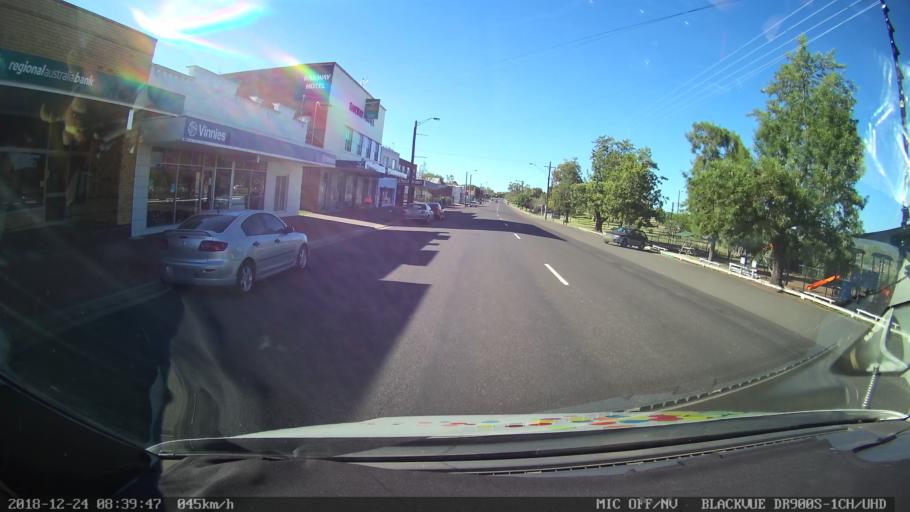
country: AU
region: New South Wales
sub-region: Liverpool Plains
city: Quirindi
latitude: -31.3504
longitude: 150.6471
